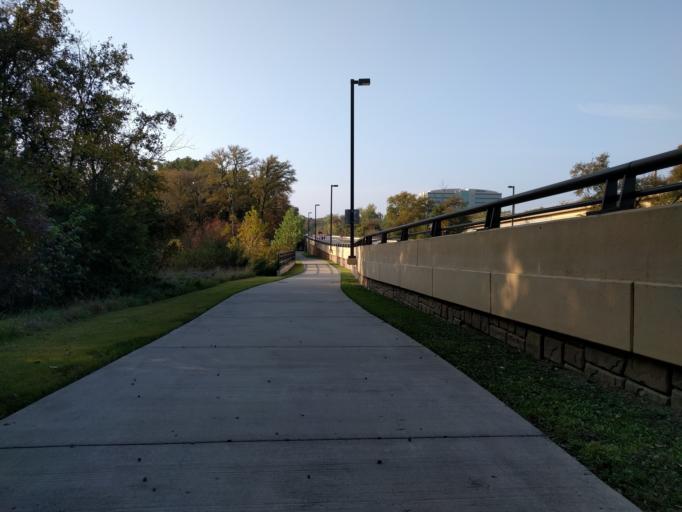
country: US
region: Texas
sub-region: Collin County
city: Plano
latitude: 32.9967
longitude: -96.7050
